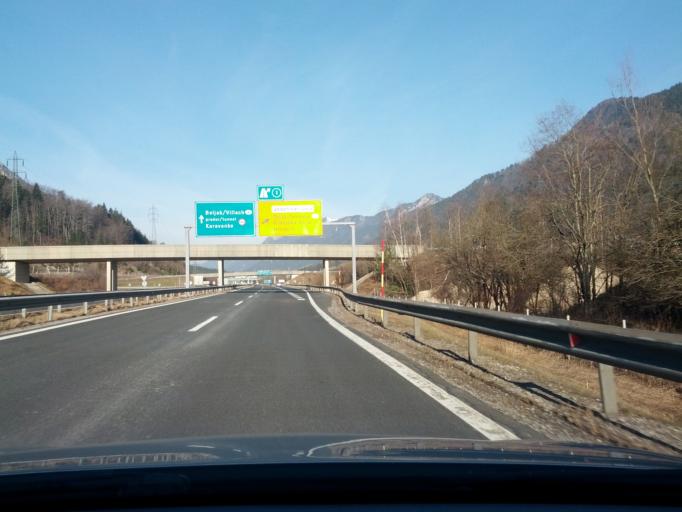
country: SI
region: Jesenice
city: Hrusica
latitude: 46.4443
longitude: 14.0156
